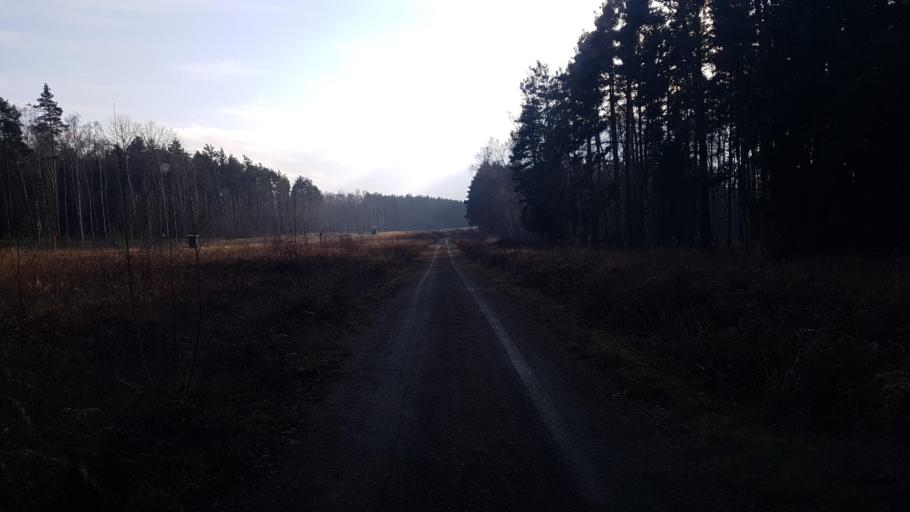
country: DE
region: Brandenburg
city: Plessa
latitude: 51.5245
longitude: 13.6803
